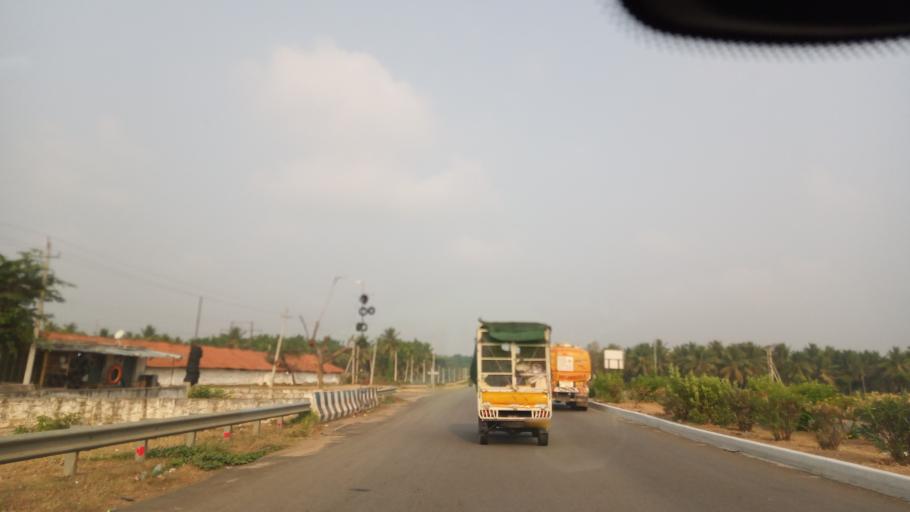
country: IN
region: Karnataka
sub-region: Tumkur
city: Kunigal
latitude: 13.0203
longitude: 77.0643
